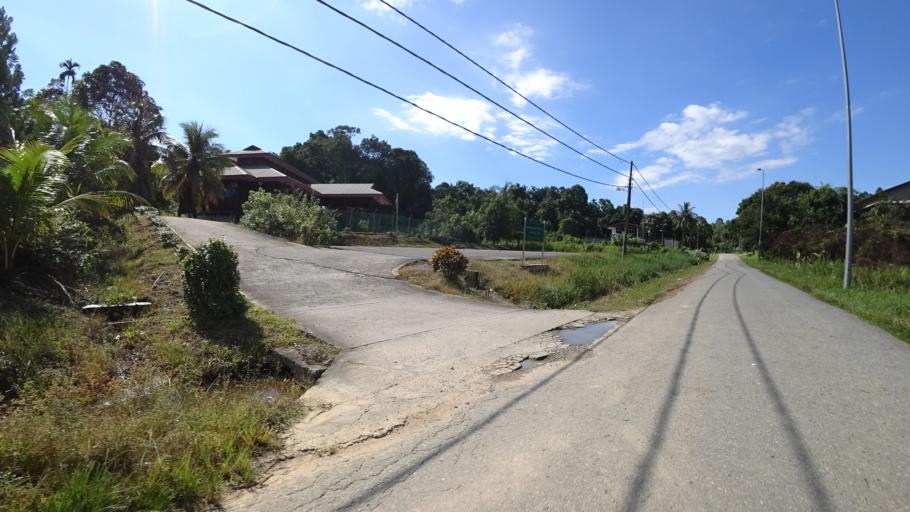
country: BN
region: Tutong
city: Tutong
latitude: 4.7418
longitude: 114.7889
